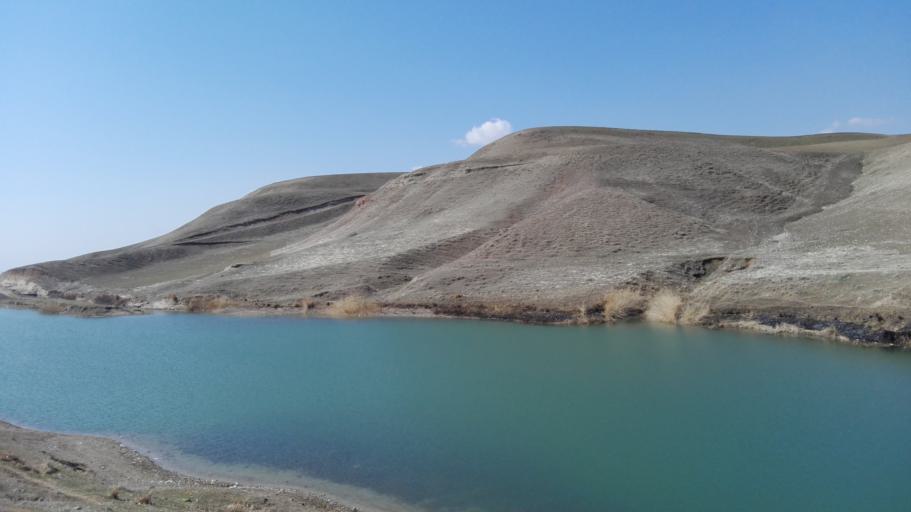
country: TR
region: Batman
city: Demiryol
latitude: 37.9359
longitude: 41.1655
